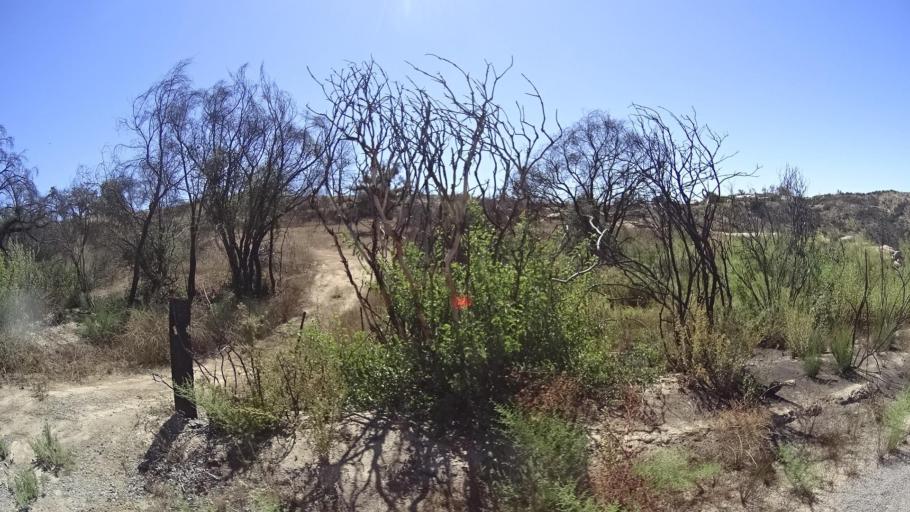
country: US
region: California
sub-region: San Diego County
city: Alpine
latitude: 32.7717
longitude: -116.7651
